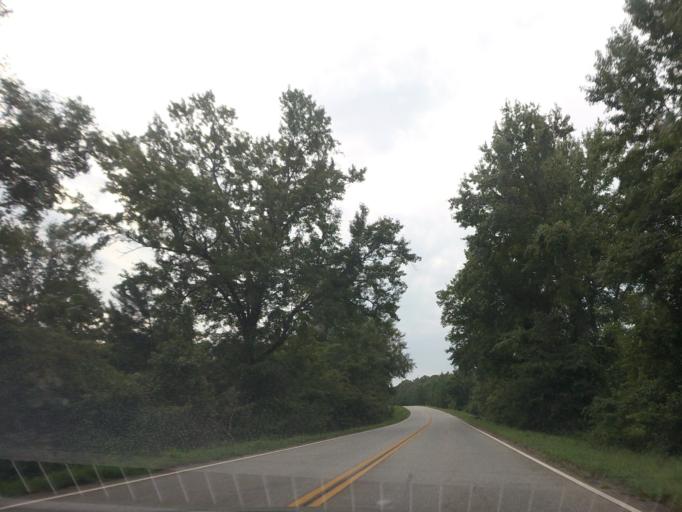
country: US
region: Georgia
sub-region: Twiggs County
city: Jeffersonville
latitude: 32.7147
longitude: -83.3889
